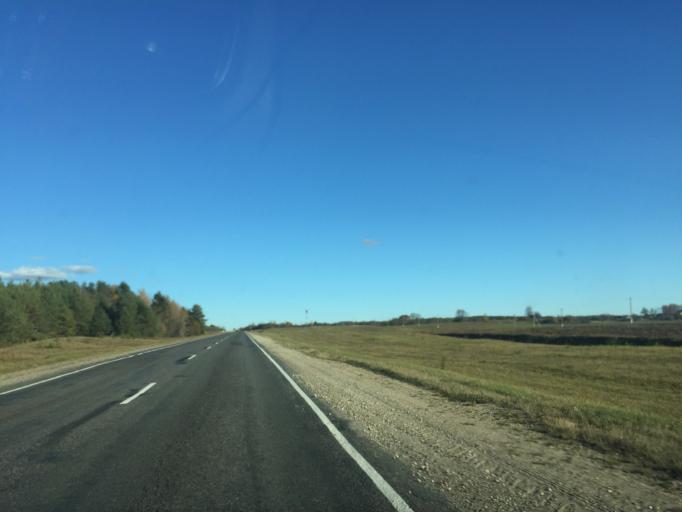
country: BY
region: Vitebsk
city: Dzisna
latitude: 55.2390
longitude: 28.0487
